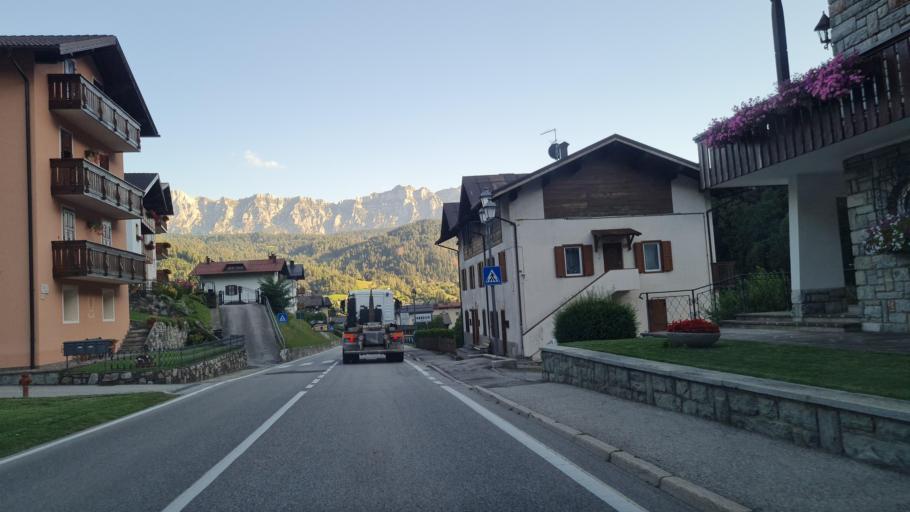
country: IT
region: Trentino-Alto Adige
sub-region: Provincia di Trento
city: Siror
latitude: 46.1862
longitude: 11.8307
